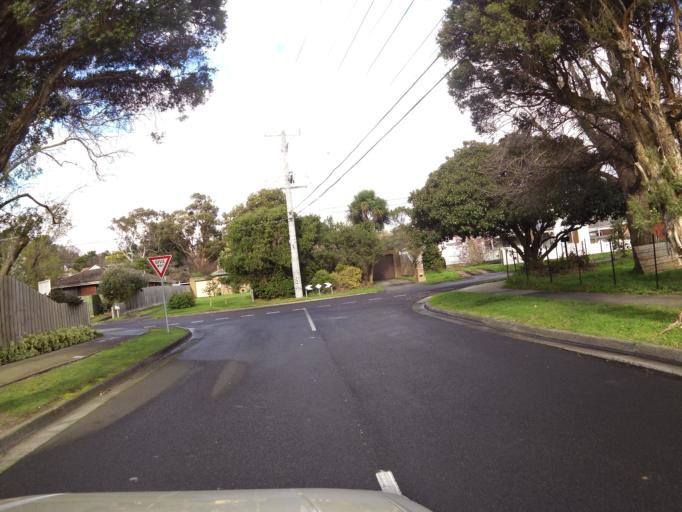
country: AU
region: Victoria
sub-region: Knox
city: Ferntree Gully
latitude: -37.8982
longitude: 145.3002
